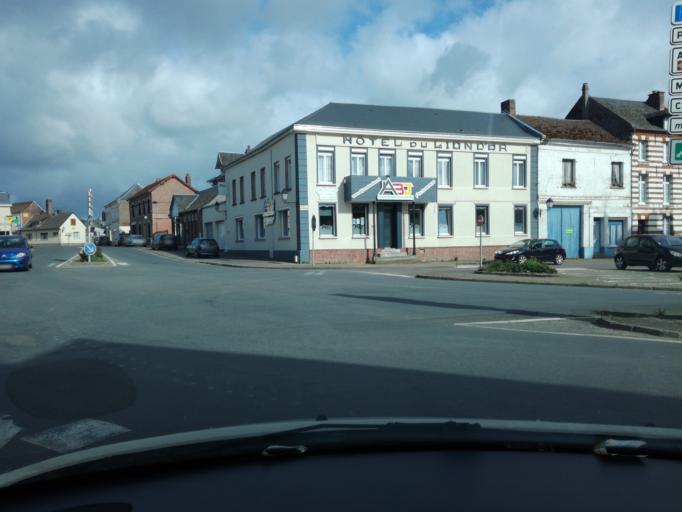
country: FR
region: Picardie
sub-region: Departement de la Somme
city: Hornoy-le-Bourg
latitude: 49.8464
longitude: 1.9025
